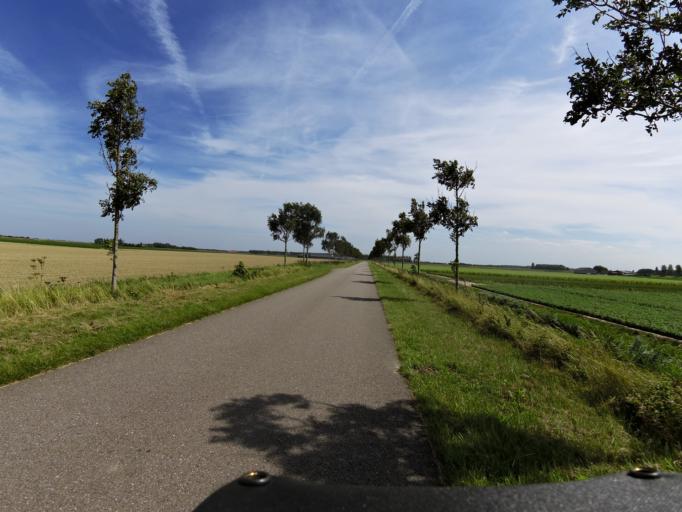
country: NL
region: South Holland
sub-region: Gemeente Goeree-Overflakkee
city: Dirksland
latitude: 51.7871
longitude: 4.0705
